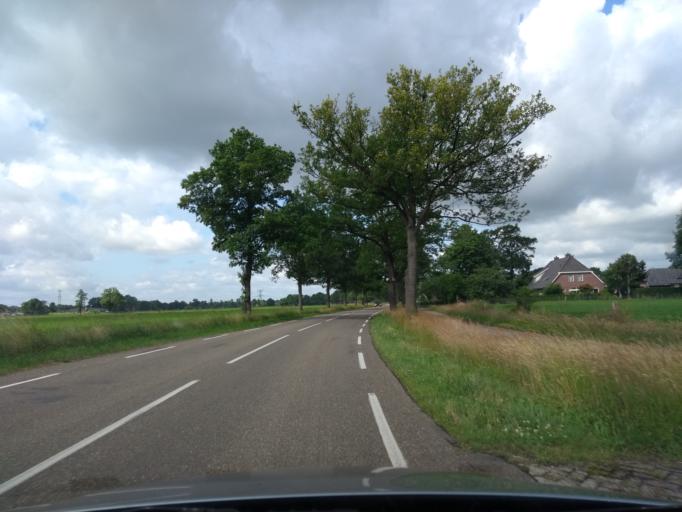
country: NL
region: Overijssel
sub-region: Gemeente Twenterand
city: Den Ham
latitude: 52.4232
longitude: 6.4961
